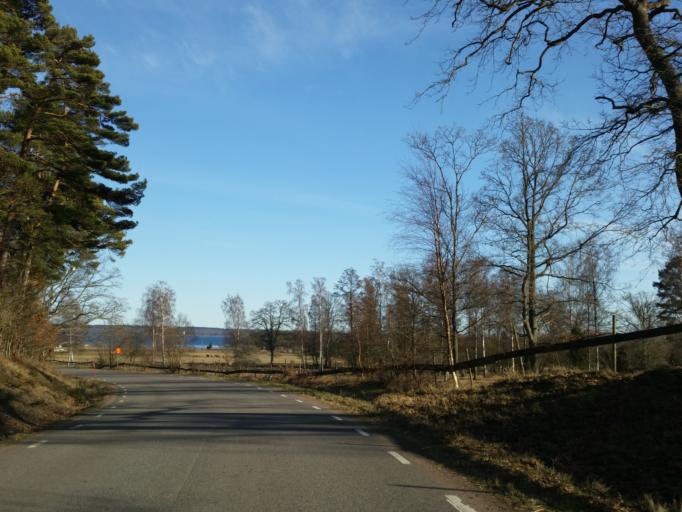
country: SE
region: Kalmar
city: Faerjestaden
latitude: 56.7744
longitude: 16.4590
